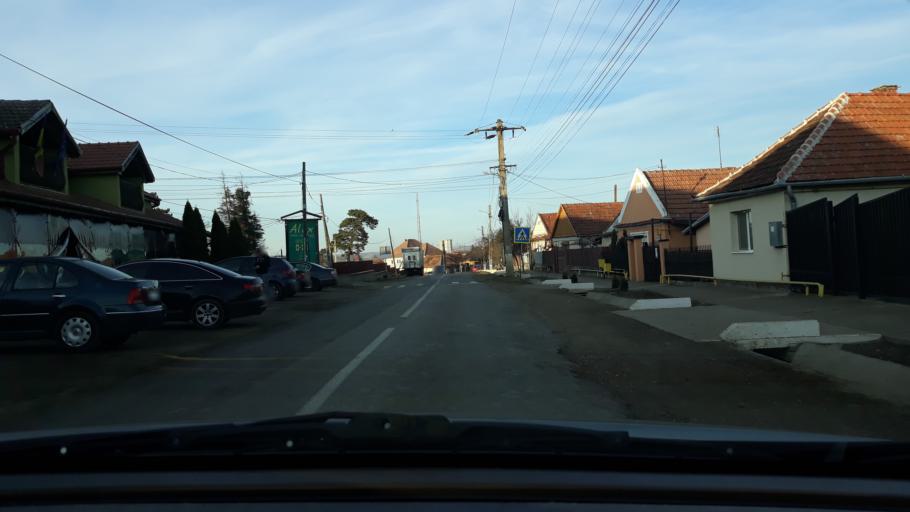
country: RO
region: Bihor
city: Foglas
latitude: 47.2512
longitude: 22.5329
